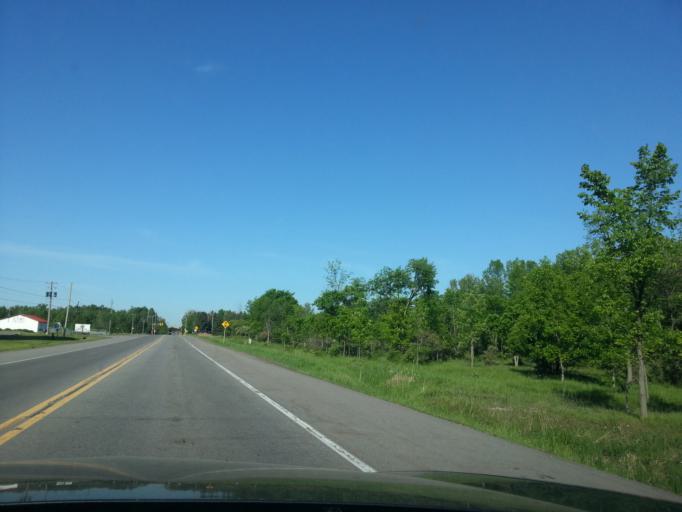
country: CA
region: Ontario
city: Bells Corners
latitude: 45.3467
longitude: -75.8767
